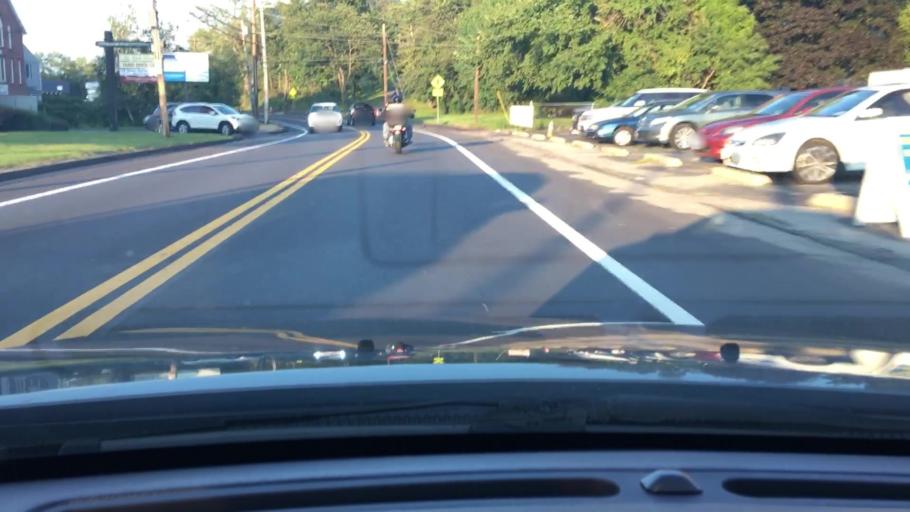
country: US
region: Massachusetts
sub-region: Worcester County
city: Grafton
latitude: 42.2289
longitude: -71.7203
